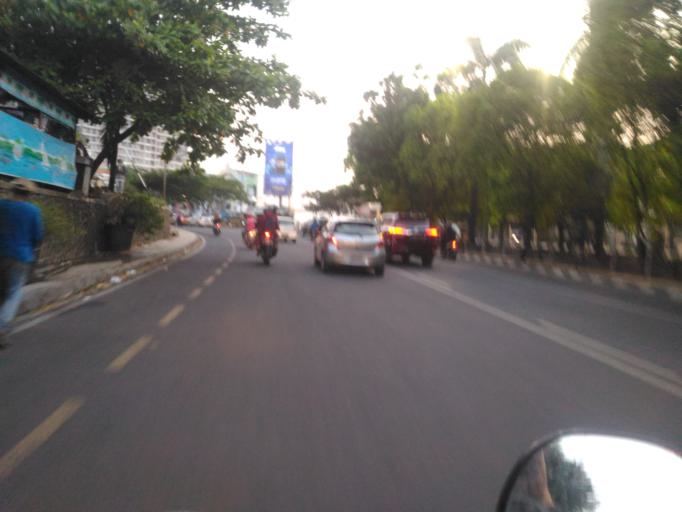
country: ID
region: West Java
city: Depok
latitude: -6.3575
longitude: 106.8330
